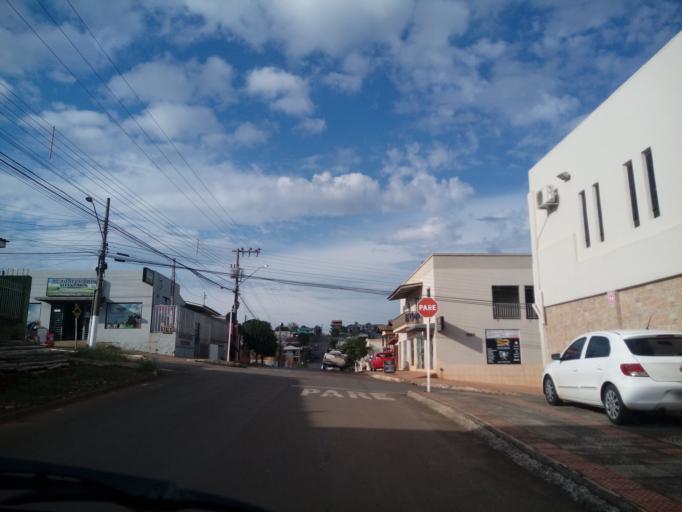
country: BR
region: Santa Catarina
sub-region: Chapeco
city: Chapeco
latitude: -27.0948
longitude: -52.5913
